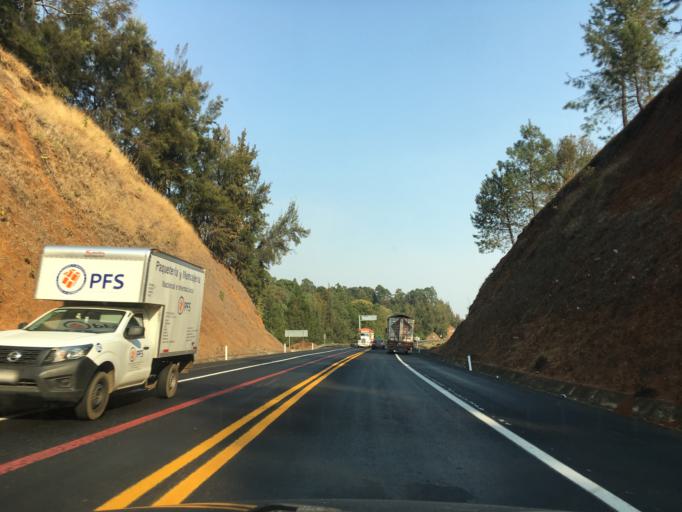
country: MX
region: Michoacan
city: Tingambato
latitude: 19.4460
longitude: -101.8507
